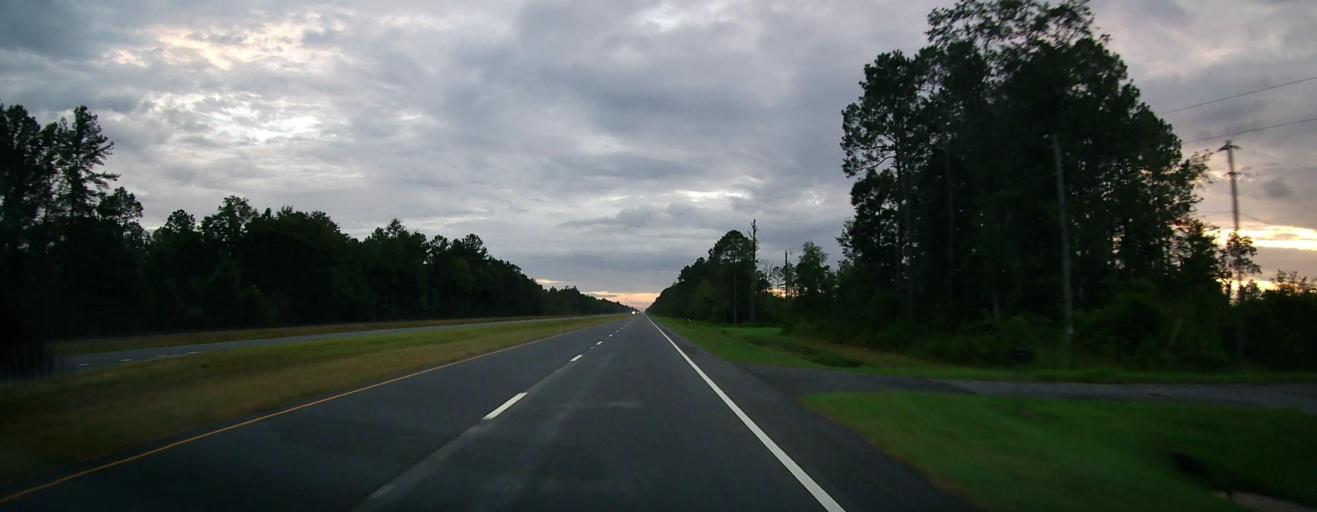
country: US
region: Georgia
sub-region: Lowndes County
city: Valdosta
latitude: 30.8836
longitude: -83.1421
